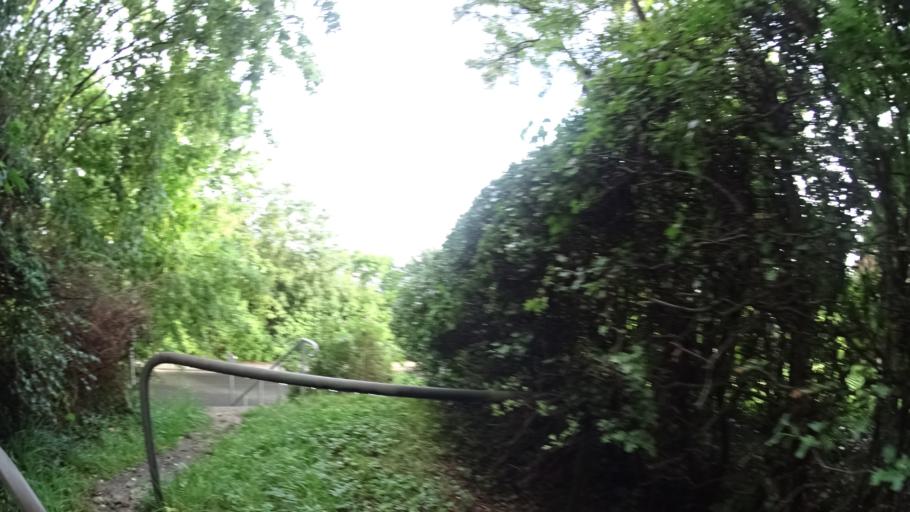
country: DK
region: Central Jutland
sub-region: Arhus Kommune
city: Stavtrup
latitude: 56.1229
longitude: 10.1626
